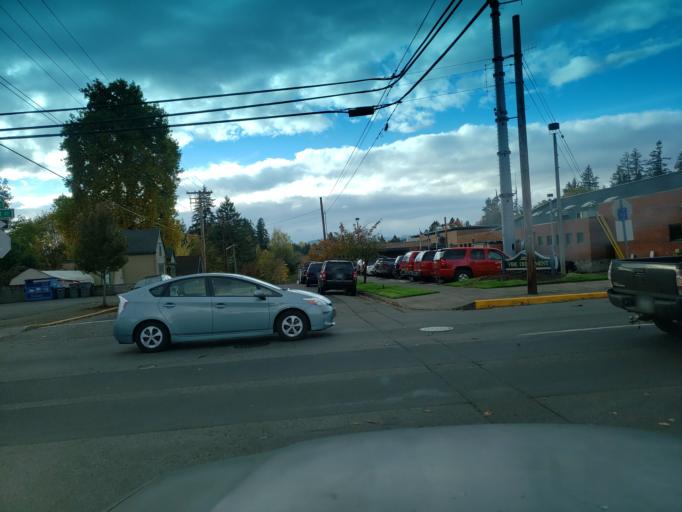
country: US
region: Oregon
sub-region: Yamhill County
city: McMinnville
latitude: 45.2086
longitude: -123.1978
